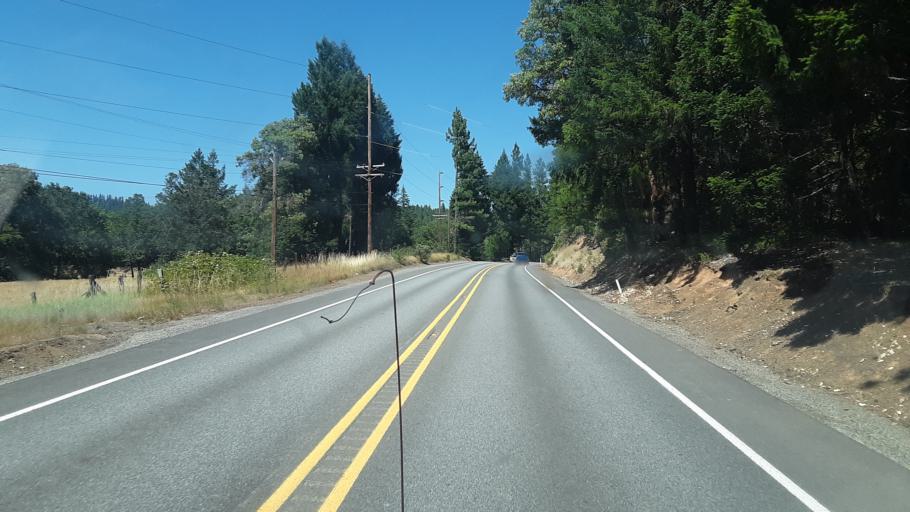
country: US
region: Oregon
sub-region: Josephine County
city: Cave Junction
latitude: 42.3140
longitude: -123.6058
